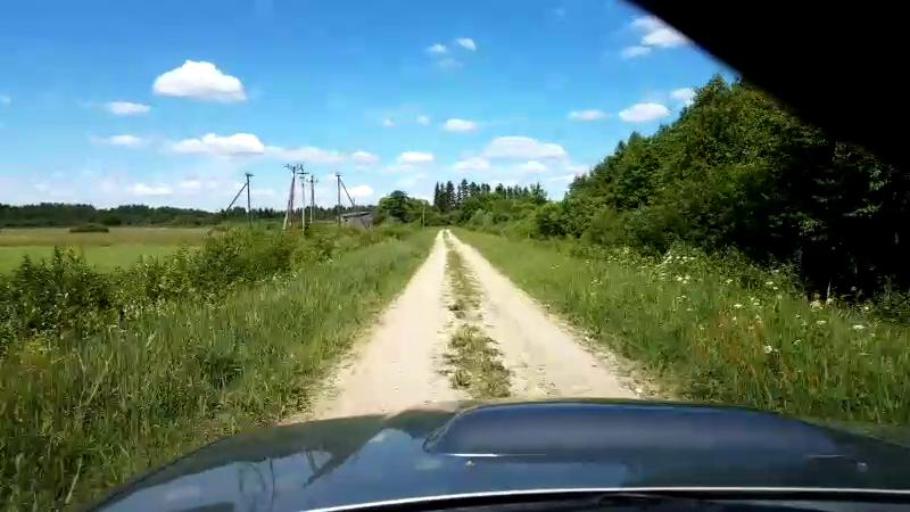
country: EE
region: Paernumaa
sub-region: Halinga vald
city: Parnu-Jaagupi
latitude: 58.5414
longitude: 24.5312
